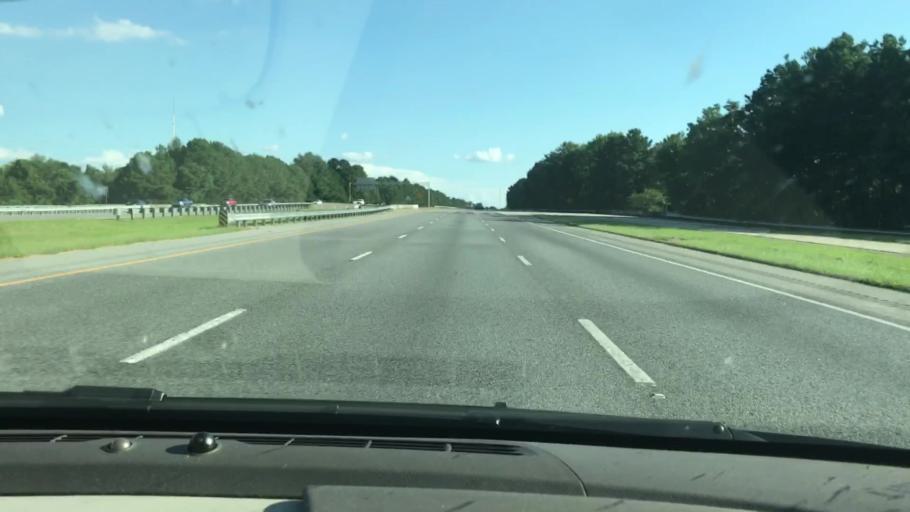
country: US
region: Alabama
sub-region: Russell County
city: Phenix City
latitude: 32.5408
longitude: -84.9604
